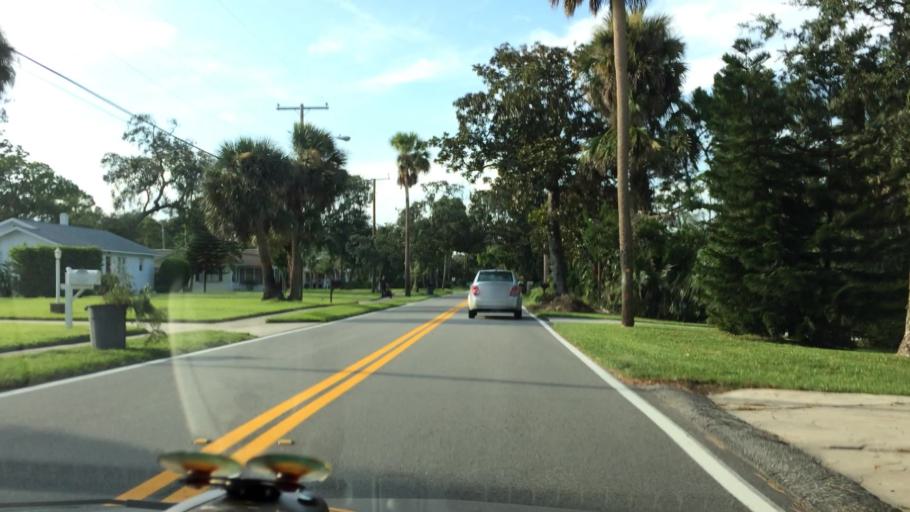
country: US
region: Florida
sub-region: Volusia County
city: Ormond Beach
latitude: 29.2939
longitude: -81.0593
